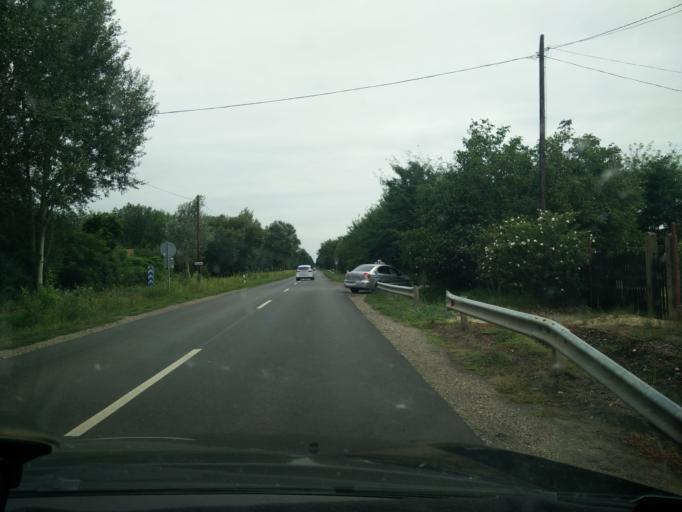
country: HU
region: Hajdu-Bihar
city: Debrecen
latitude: 47.5297
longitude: 21.7147
